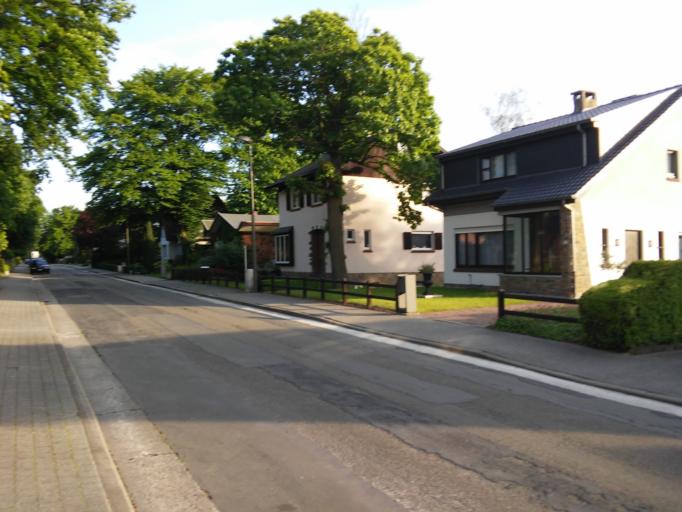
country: BE
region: Flanders
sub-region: Provincie Antwerpen
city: Rumst
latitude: 51.0466
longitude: 4.4400
